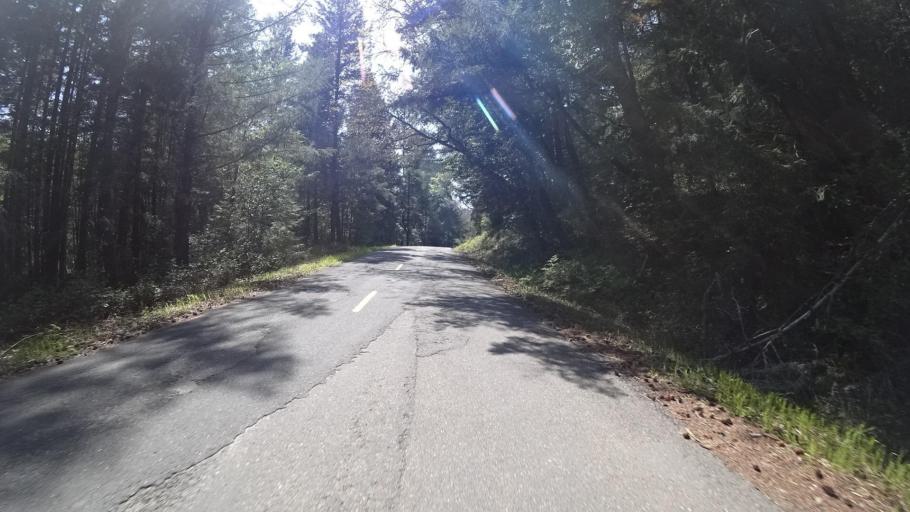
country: US
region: California
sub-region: Humboldt County
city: Redway
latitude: 40.3349
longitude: -123.6838
